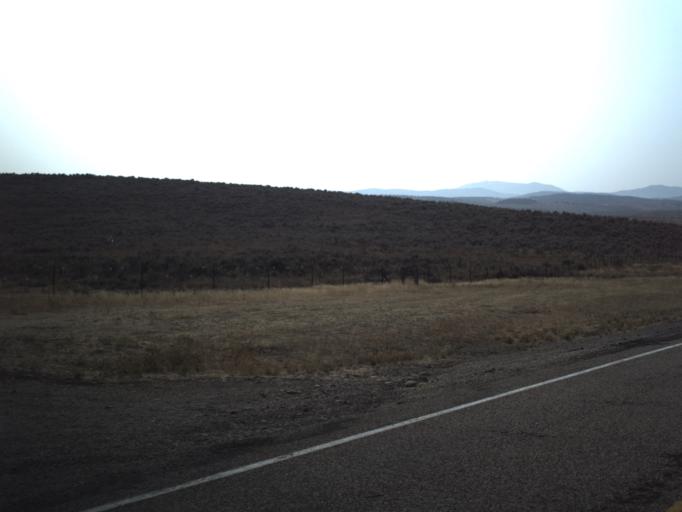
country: US
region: Utah
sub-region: Morgan County
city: Morgan
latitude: 40.9537
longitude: -111.5497
